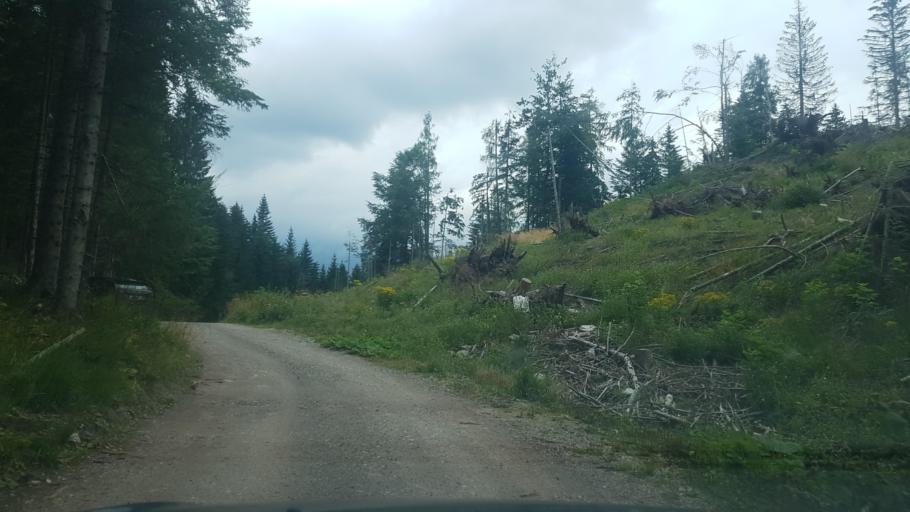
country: IT
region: Friuli Venezia Giulia
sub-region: Provincia di Udine
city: Rigolato
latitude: 46.5566
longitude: 12.8168
